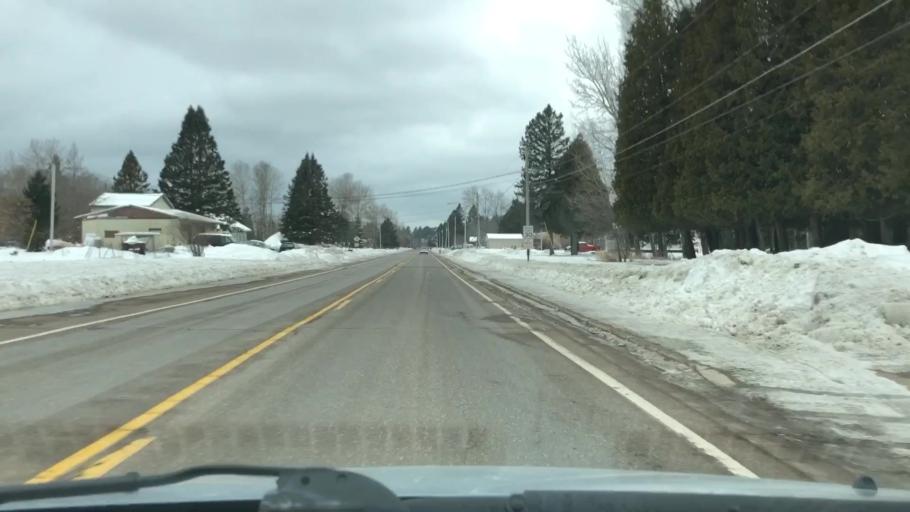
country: US
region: Minnesota
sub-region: Carlton County
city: Carlton
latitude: 46.6636
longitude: -92.3873
